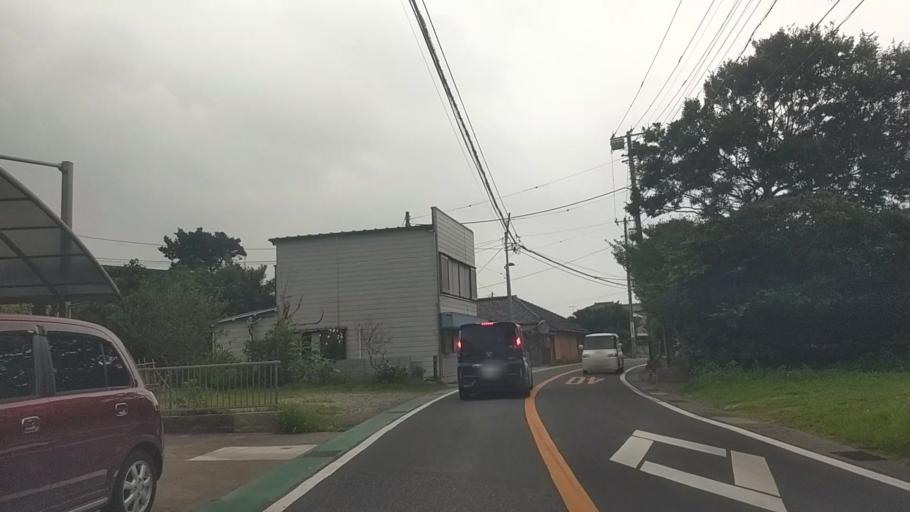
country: JP
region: Chiba
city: Tateyama
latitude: 35.1406
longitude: 139.8421
